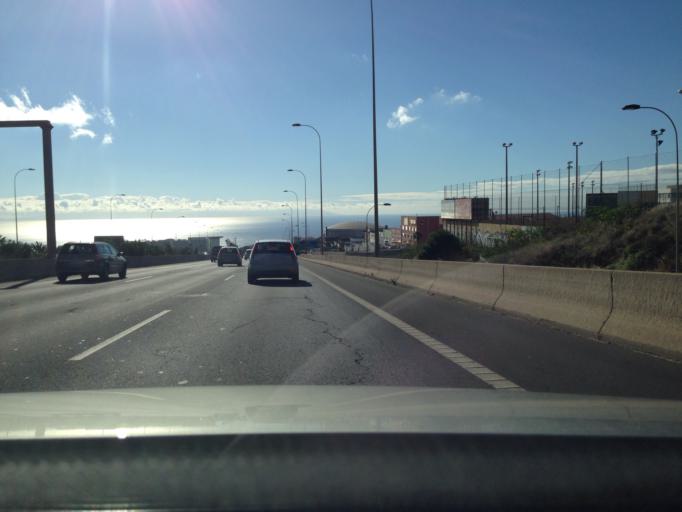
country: ES
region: Canary Islands
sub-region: Provincia de Santa Cruz de Tenerife
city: La Laguna
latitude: 28.4636
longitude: -16.3009
